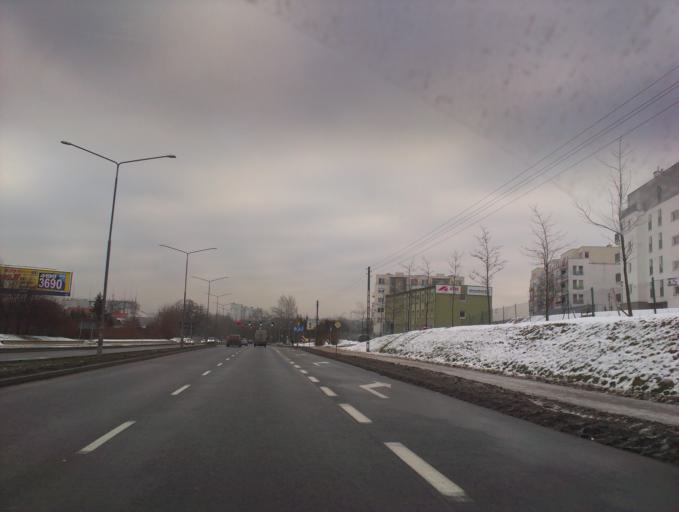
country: PL
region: Greater Poland Voivodeship
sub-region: Poznan
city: Poznan
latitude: 52.4309
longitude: 16.9543
